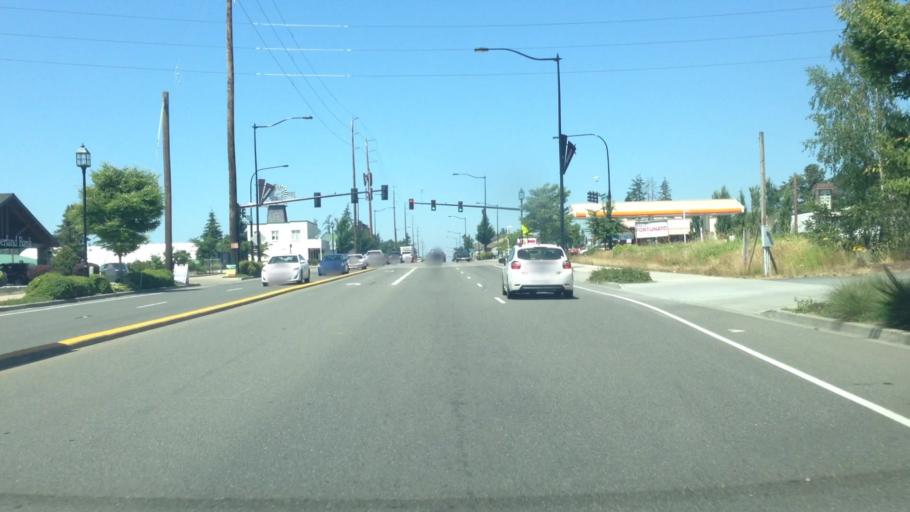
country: US
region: Washington
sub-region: Pierce County
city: Edgewood
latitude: 47.2346
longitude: -122.2939
